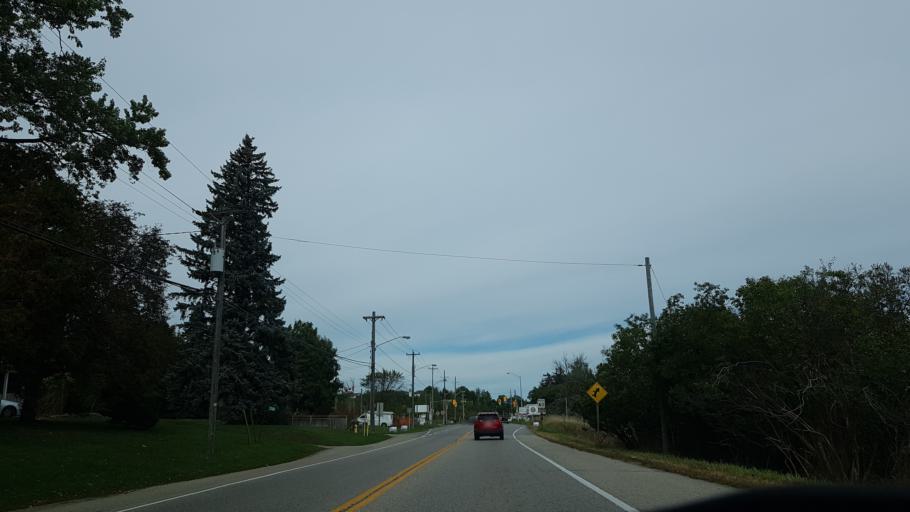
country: CA
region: Ontario
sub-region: Wellington County
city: Guelph
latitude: 43.5174
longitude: -80.2682
